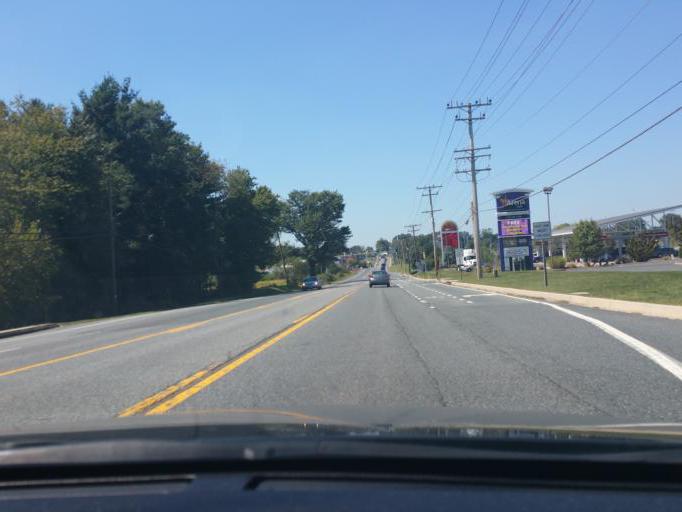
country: US
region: Maryland
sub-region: Harford County
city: South Bel Air
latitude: 39.5551
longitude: -76.2766
